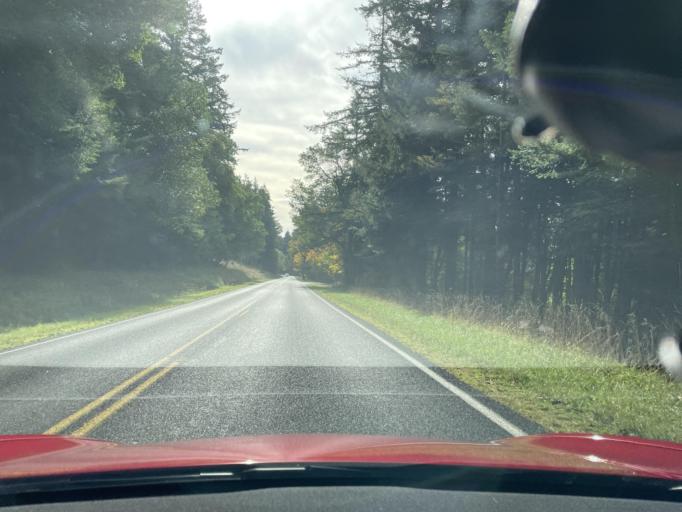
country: US
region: Washington
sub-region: San Juan County
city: Friday Harbor
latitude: 48.5833
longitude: -123.1445
